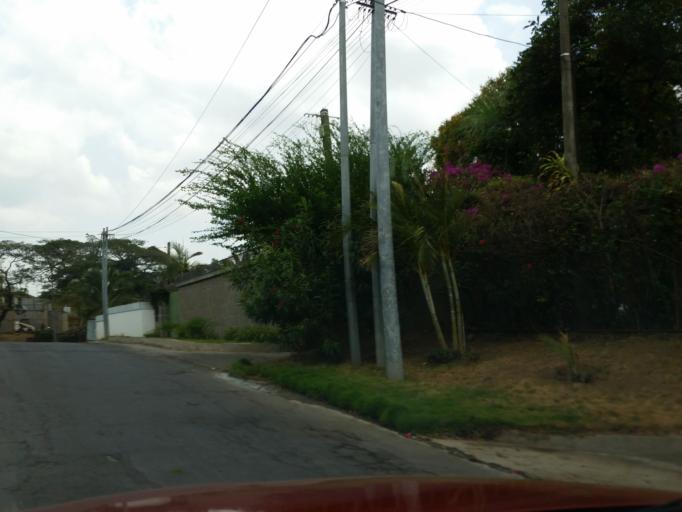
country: NI
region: Managua
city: Managua
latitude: 12.0904
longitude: -86.2457
